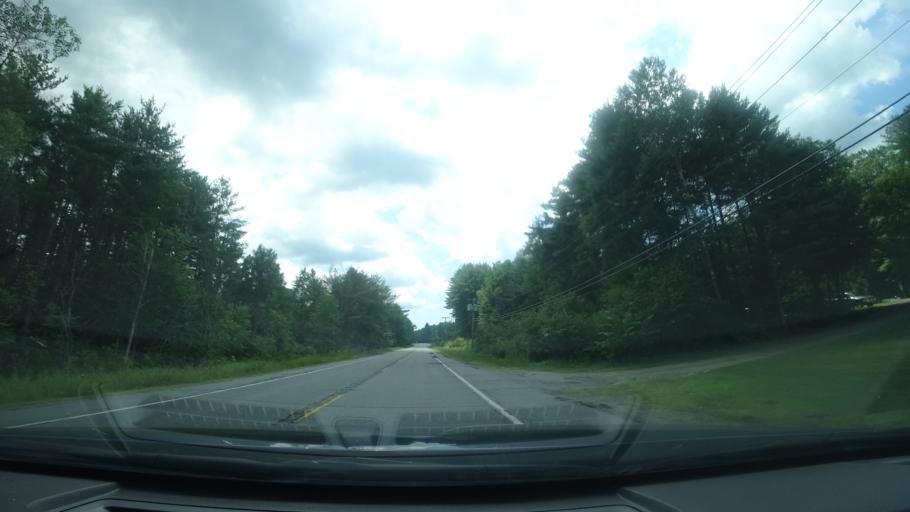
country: US
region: New York
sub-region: Warren County
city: Warrensburg
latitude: 43.5194
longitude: -73.7900
